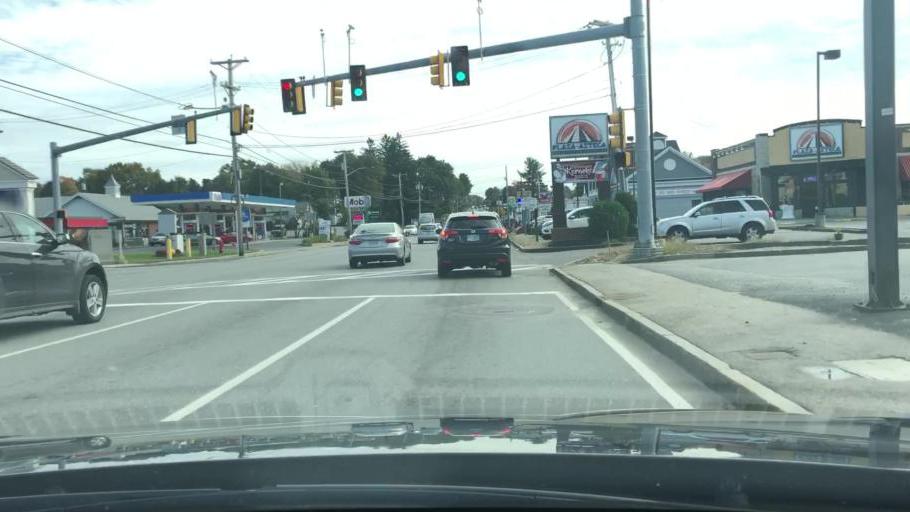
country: US
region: Massachusetts
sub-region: Essex County
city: Methuen
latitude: 42.7411
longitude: -71.1979
